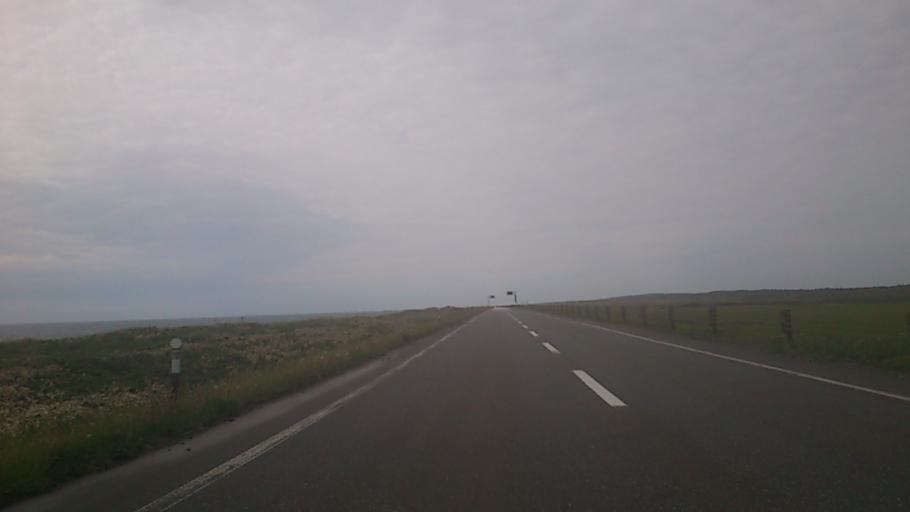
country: JP
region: Hokkaido
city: Makubetsu
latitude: 45.0405
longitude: 141.6590
